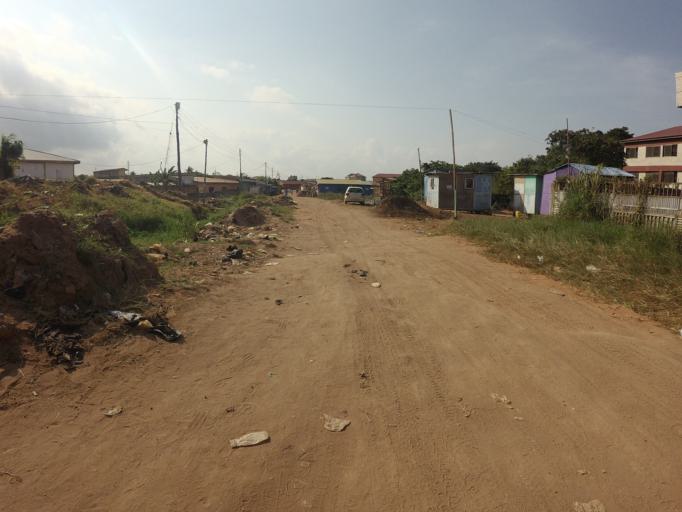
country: GH
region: Greater Accra
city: Dome
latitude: 5.6549
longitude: -0.2655
